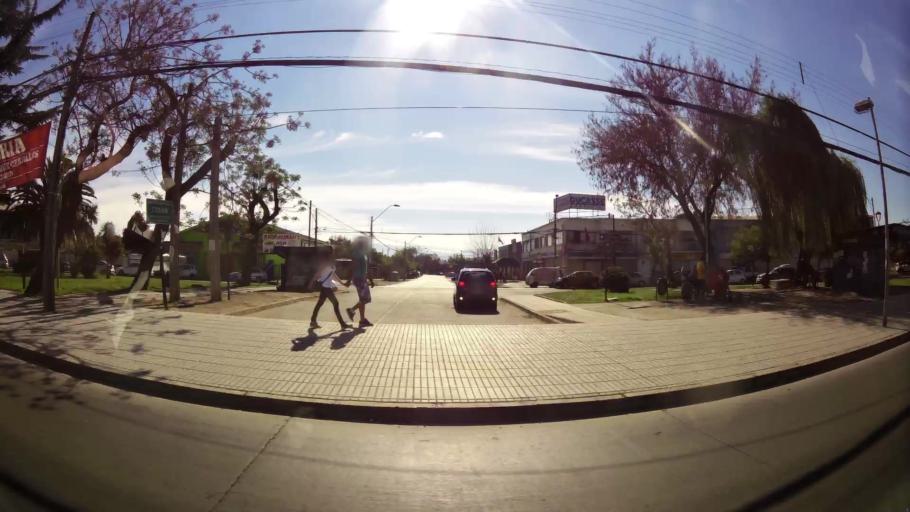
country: CL
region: Santiago Metropolitan
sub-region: Provincia de Santiago
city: Lo Prado
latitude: -33.4945
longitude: -70.7055
